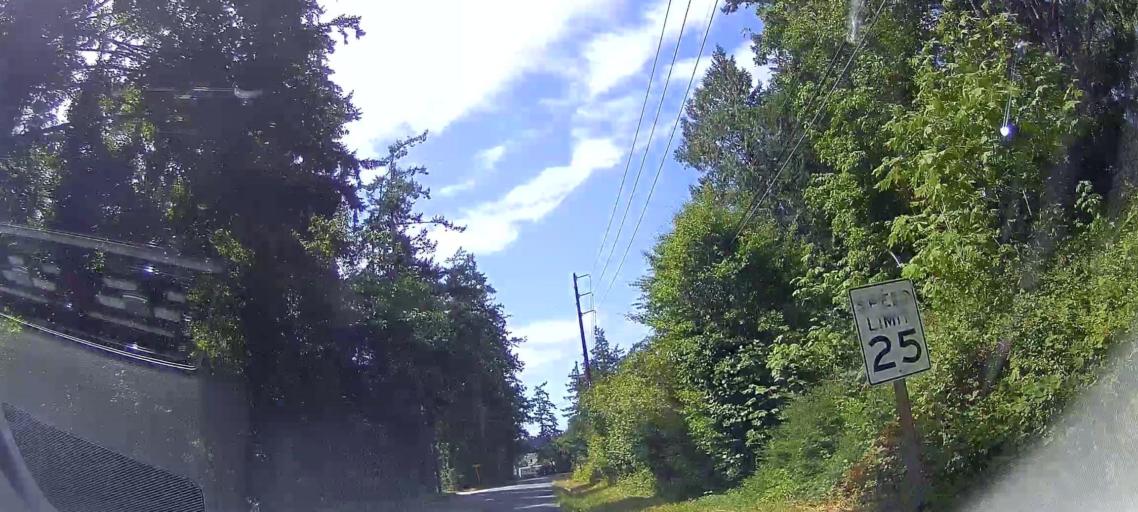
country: US
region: Washington
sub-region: Skagit County
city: Anacortes
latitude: 48.4489
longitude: -122.5673
